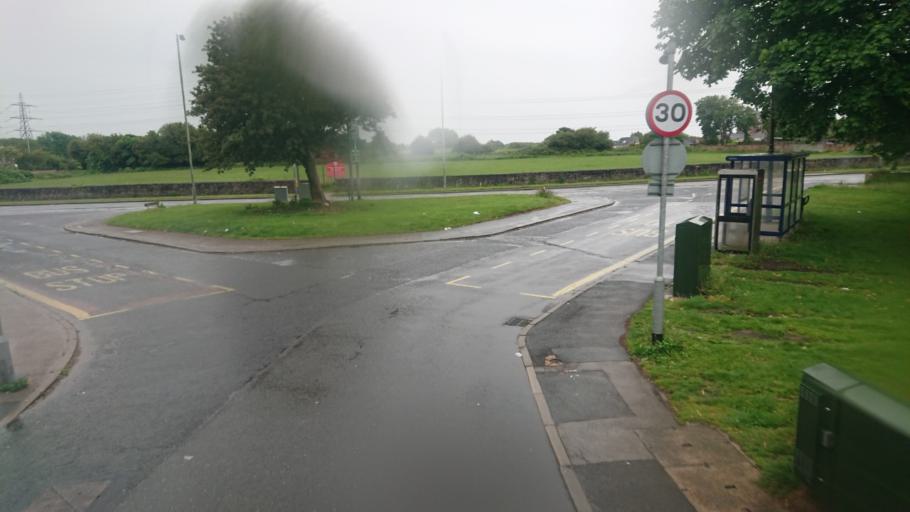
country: GB
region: England
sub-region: Lancashire
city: Morecambe
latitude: 54.0359
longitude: -2.8976
